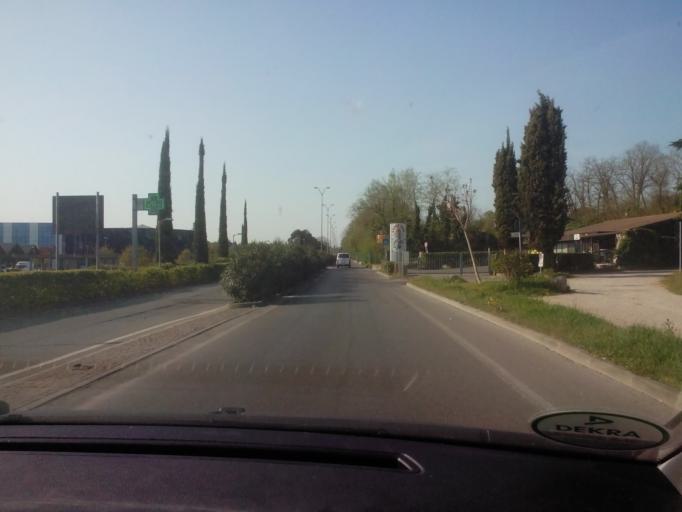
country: IT
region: Lombardy
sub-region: Provincia di Brescia
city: Desenzano del Garda
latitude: 45.4651
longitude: 10.5262
